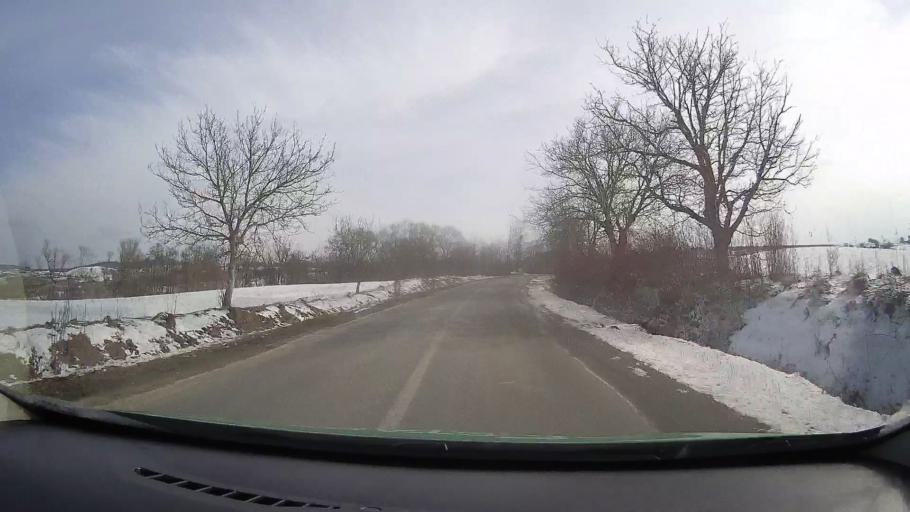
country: RO
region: Mures
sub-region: Comuna Apold
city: Apold
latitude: 46.1149
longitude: 24.8272
